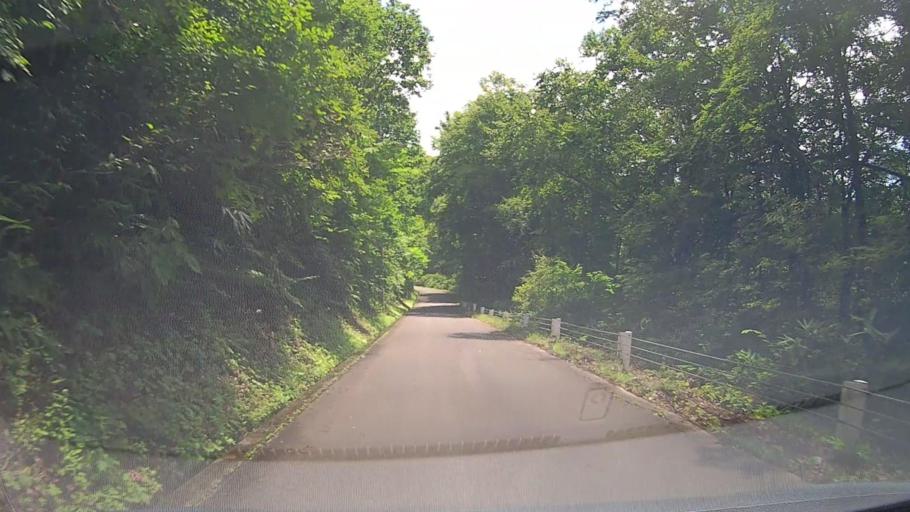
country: JP
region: Nagano
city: Iiyama
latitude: 36.9324
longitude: 138.4676
